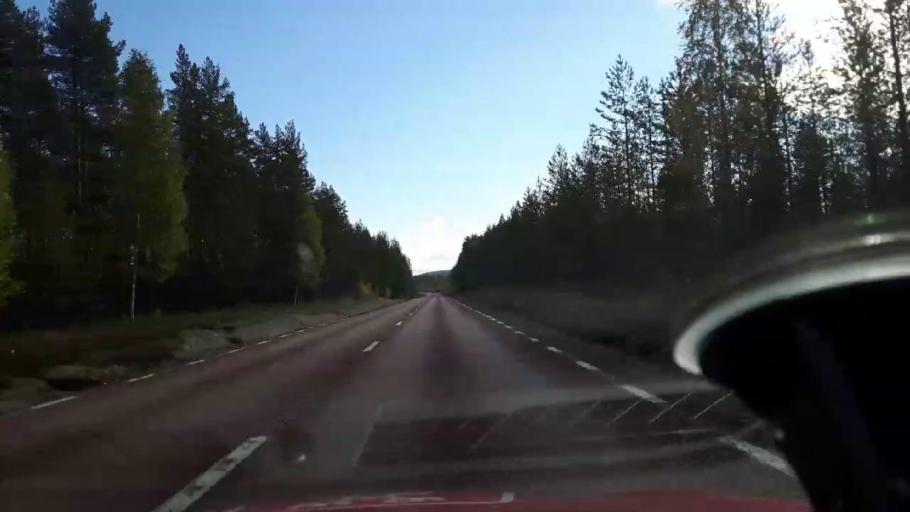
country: SE
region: Gaevleborg
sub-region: Ljusdals Kommun
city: Farila
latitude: 61.9339
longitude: 15.5285
